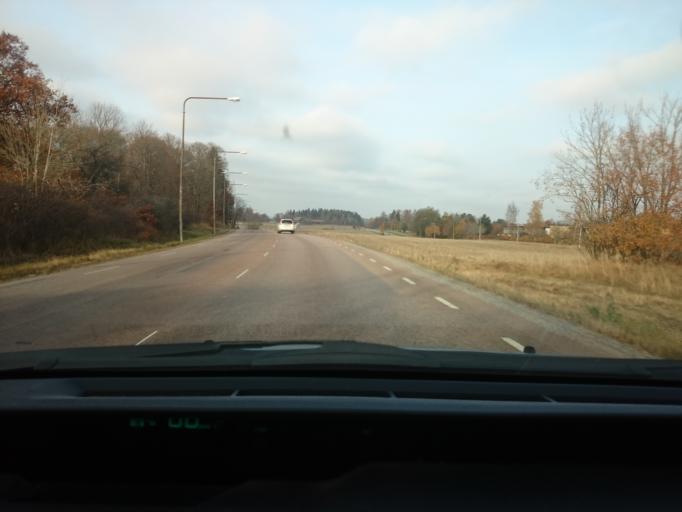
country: SE
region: Vaestmanland
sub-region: Vasteras
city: Vasteras
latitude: 59.6442
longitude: 16.5027
